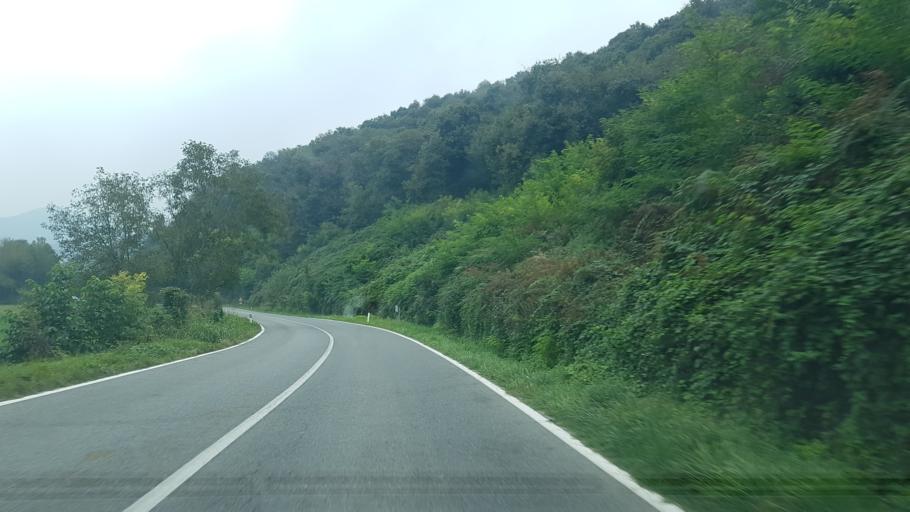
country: IT
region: Piedmont
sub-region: Provincia di Cuneo
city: Villanova Mondovi
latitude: 44.3304
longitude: 7.7863
